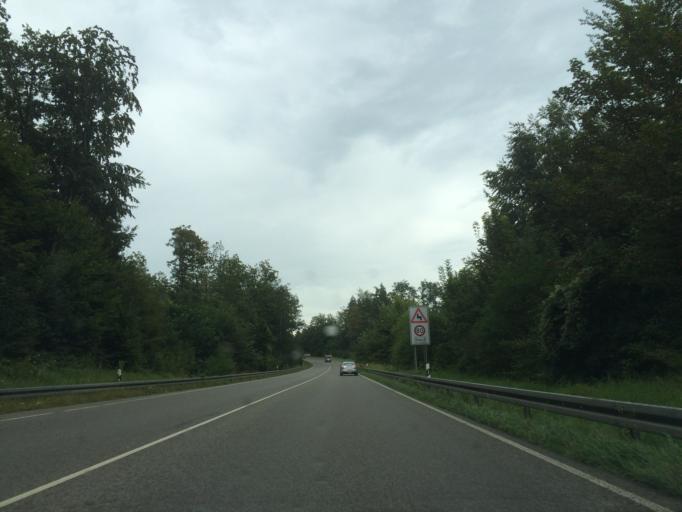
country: DE
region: Baden-Wuerttemberg
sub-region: Tuebingen Region
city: Baindt
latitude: 47.8657
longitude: 9.6854
